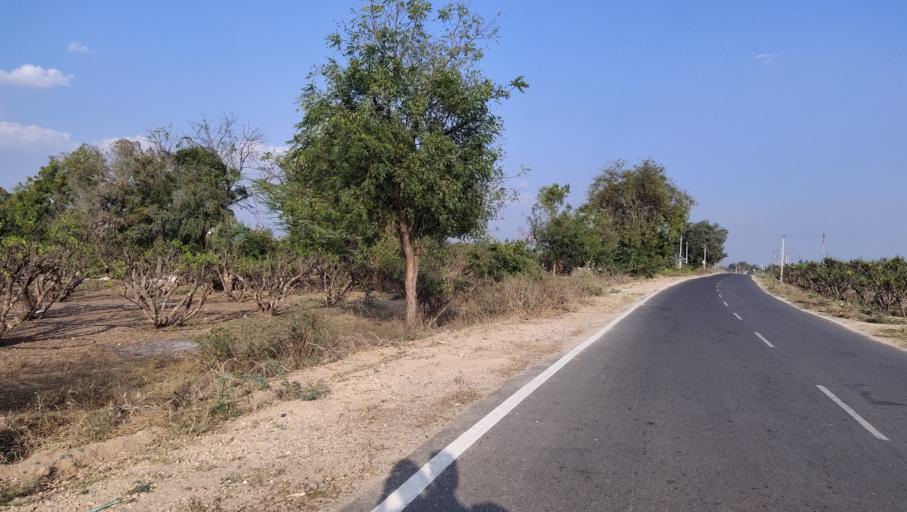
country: IN
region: Andhra Pradesh
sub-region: Anantapur
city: Tadpatri
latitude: 14.9514
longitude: 77.8831
